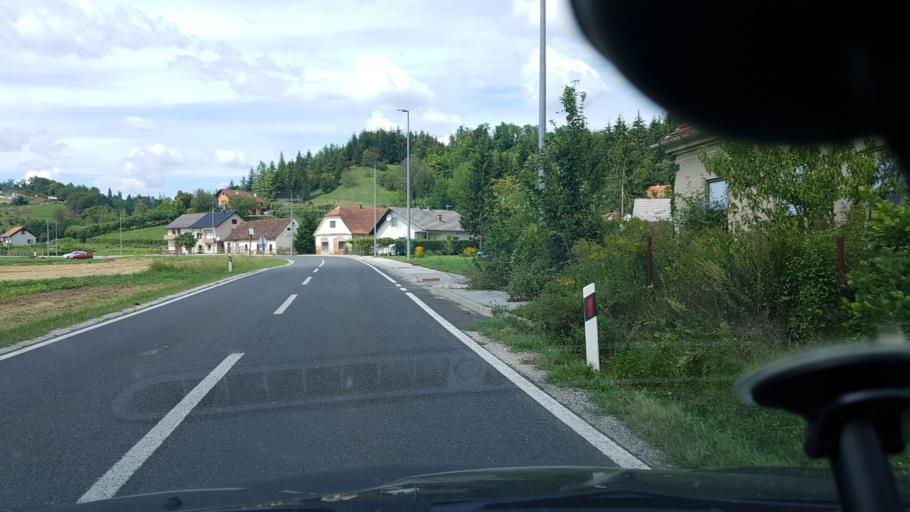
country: HR
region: Varazdinska
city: Lepoglava
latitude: 46.2289
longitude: 15.9929
